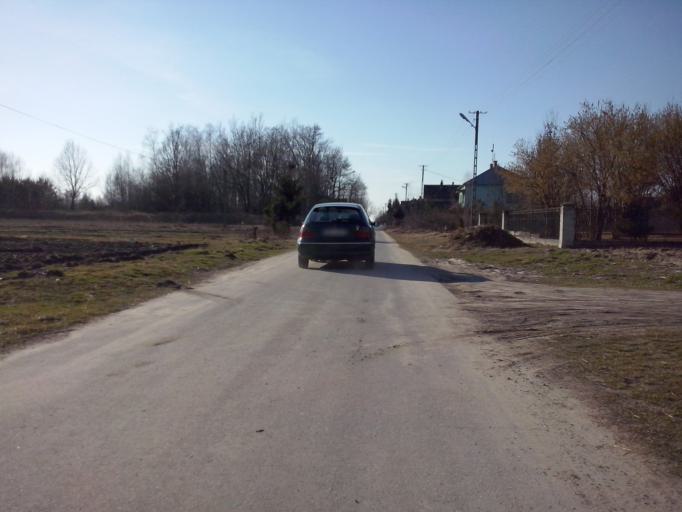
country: PL
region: Subcarpathian Voivodeship
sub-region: Powiat nizanski
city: Krzeszow
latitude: 50.4141
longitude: 22.3804
